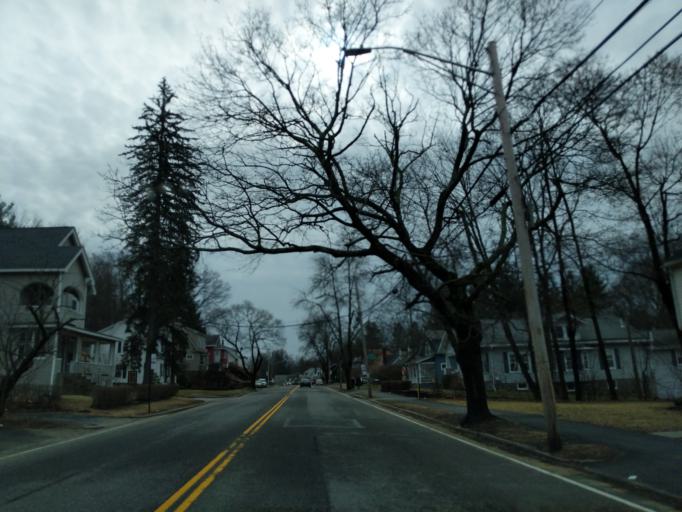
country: US
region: Massachusetts
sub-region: Worcester County
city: Worcester
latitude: 42.2739
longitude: -71.8499
